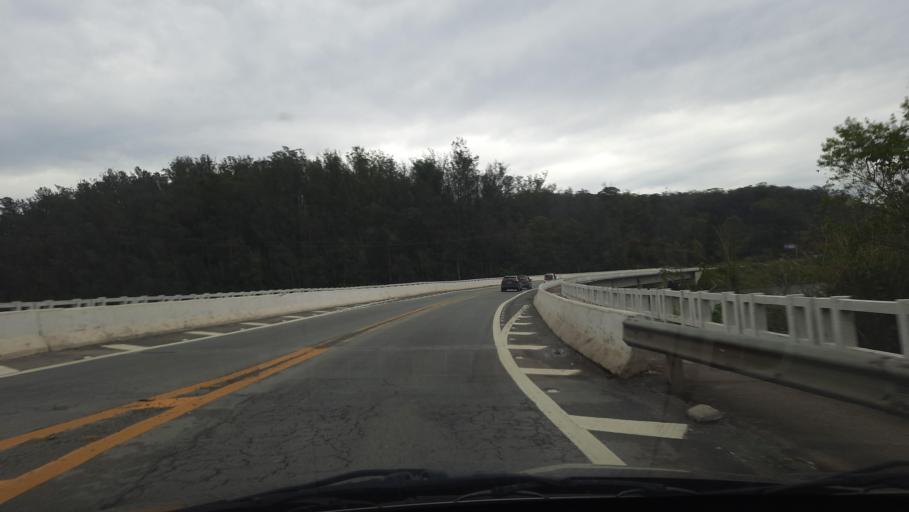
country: BR
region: Sao Paulo
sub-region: Franco Da Rocha
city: Franco da Rocha
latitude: -23.3379
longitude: -46.6600
